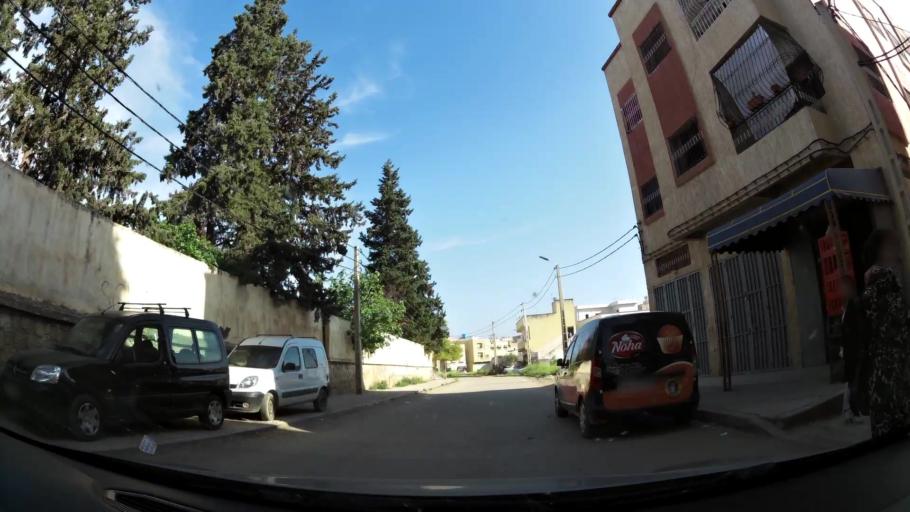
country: MA
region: Fes-Boulemane
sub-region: Fes
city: Fes
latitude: 34.0212
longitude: -5.0330
